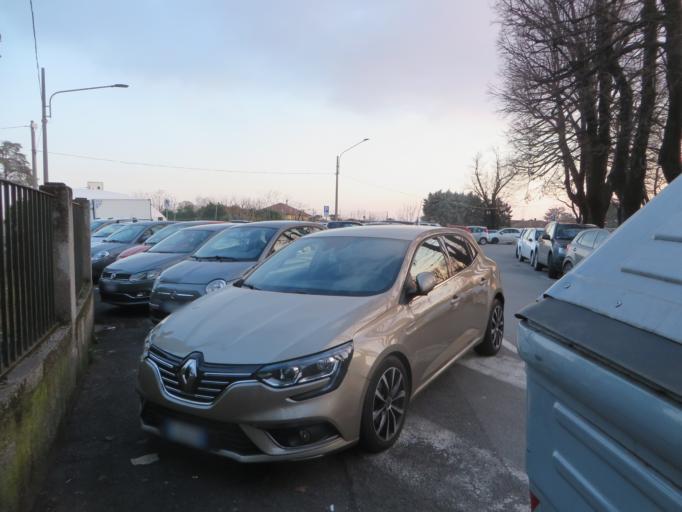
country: IT
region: Lombardy
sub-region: Provincia di Brescia
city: Brescia
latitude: 45.5336
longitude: 10.2318
